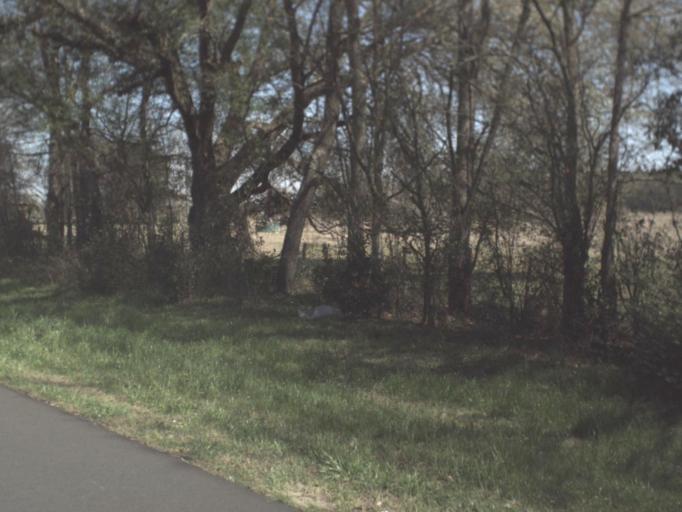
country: US
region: Florida
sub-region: Jackson County
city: Sneads
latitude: 30.7610
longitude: -85.0193
